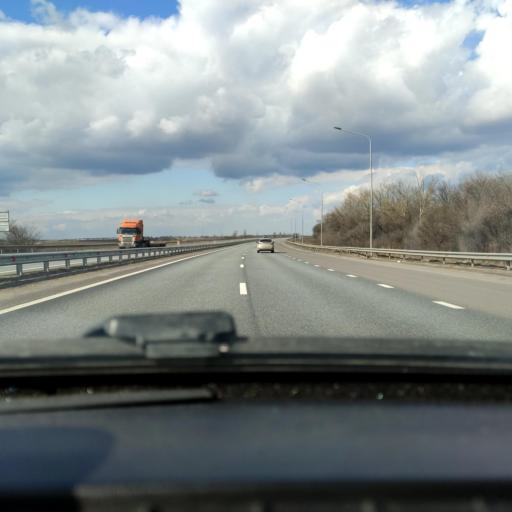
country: RU
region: Tula
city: Yefremov
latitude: 53.0169
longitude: 38.2140
